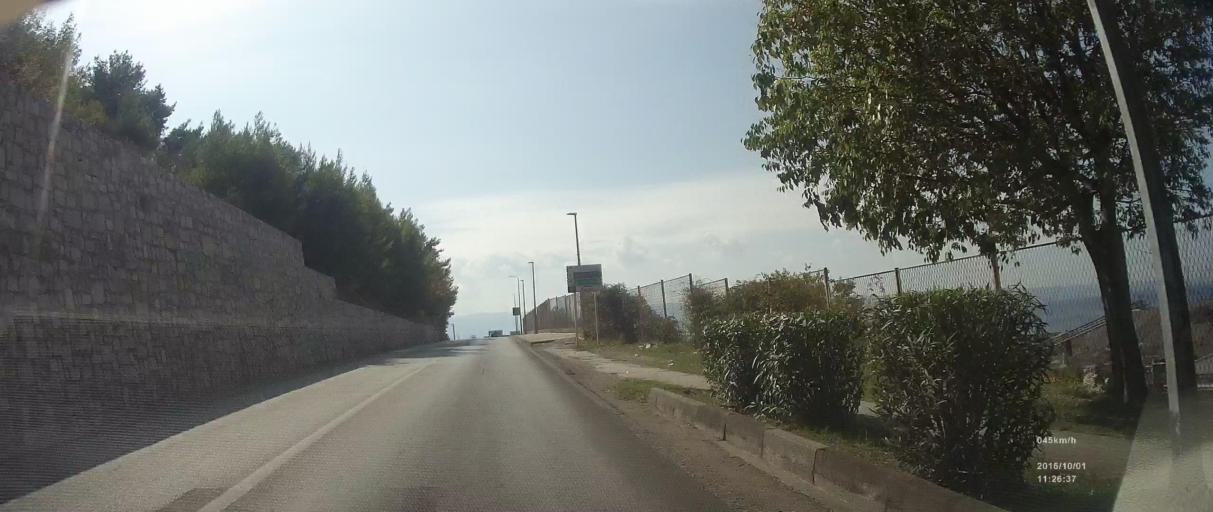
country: HR
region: Splitsko-Dalmatinska
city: Duce
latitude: 43.4417
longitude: 16.6435
